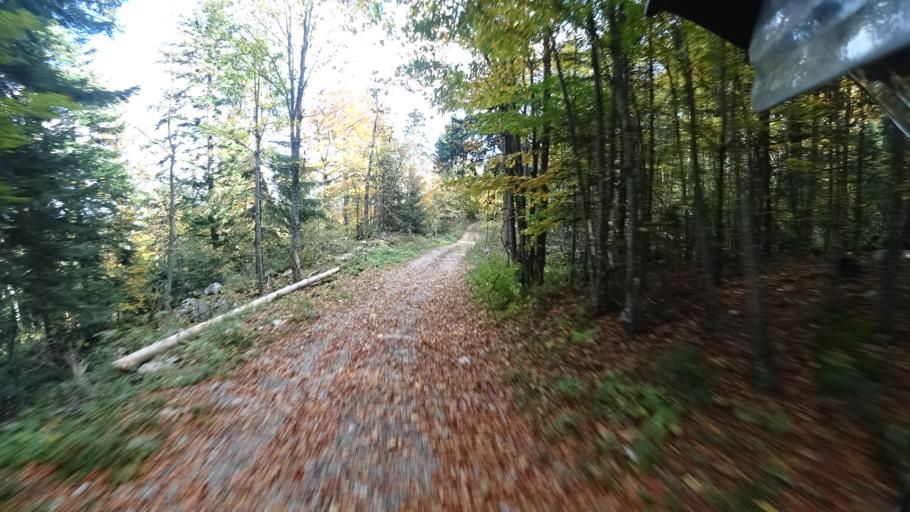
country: HR
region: Karlovacka
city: Plaski
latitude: 45.0579
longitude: 15.3427
